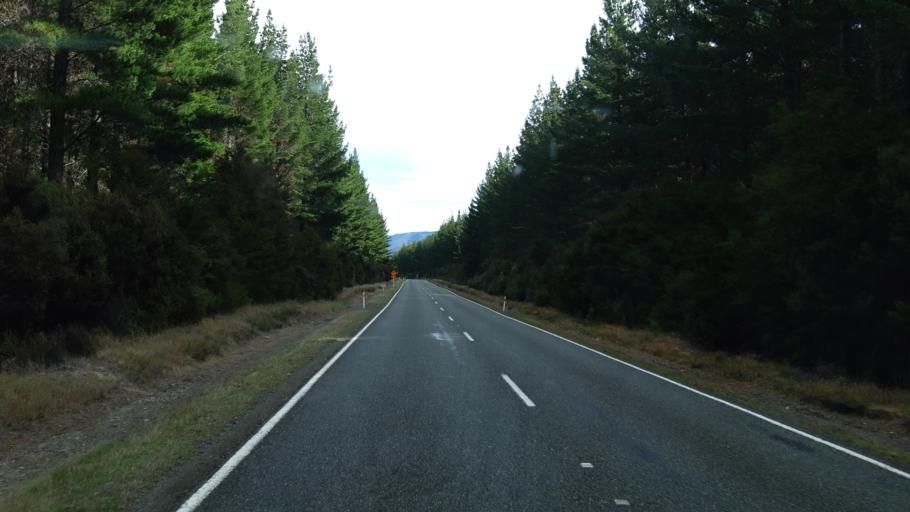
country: NZ
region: Tasman
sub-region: Tasman District
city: Wakefield
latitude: -41.7189
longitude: 173.0691
